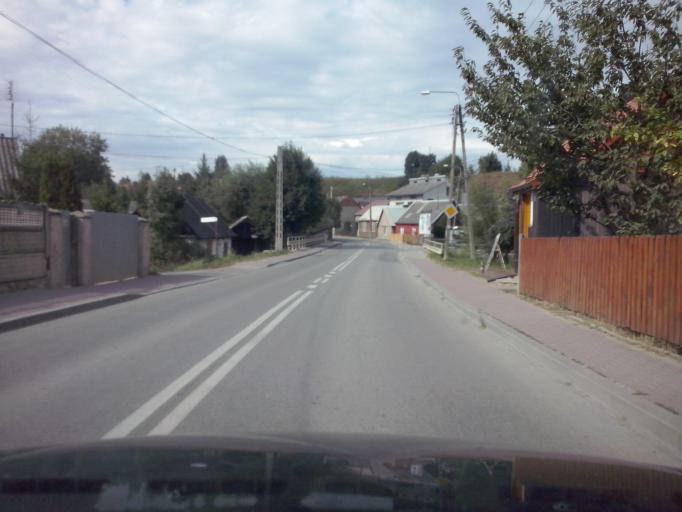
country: PL
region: Swietokrzyskie
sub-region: Powiat kielecki
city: Lagow
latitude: 50.7796
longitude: 21.0850
